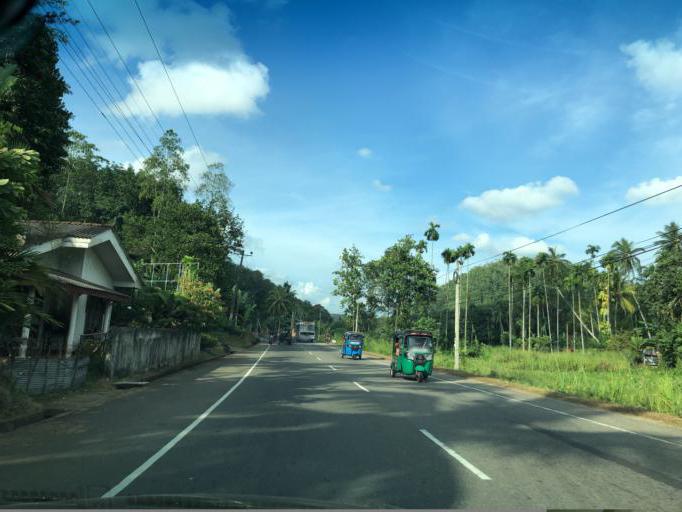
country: LK
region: Western
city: Horawala Junction
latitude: 6.5194
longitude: 80.0808
